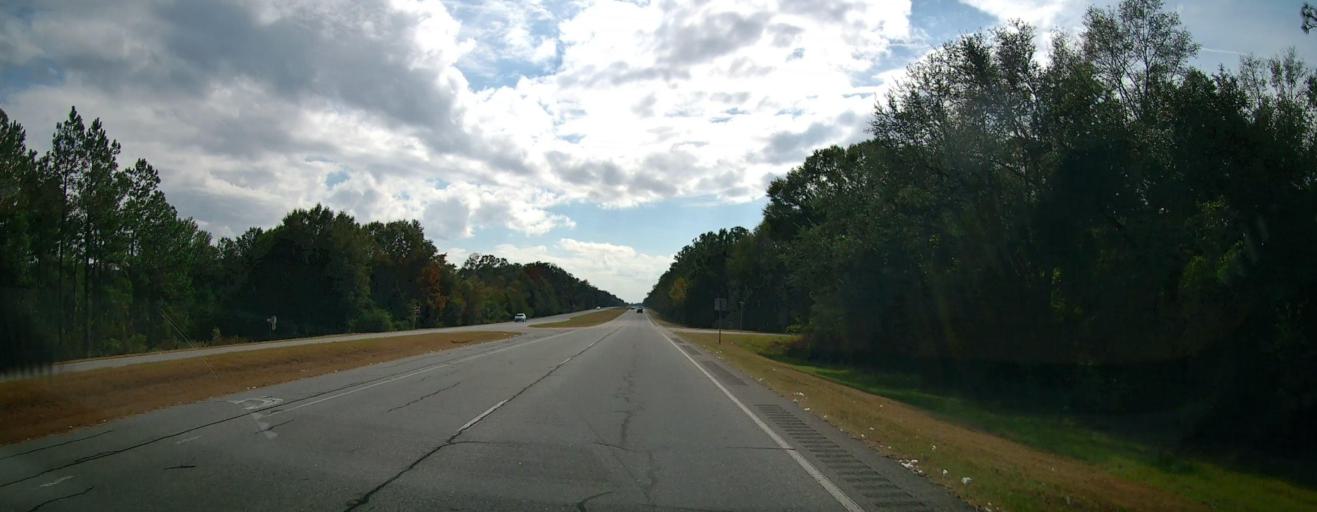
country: US
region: Georgia
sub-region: Mitchell County
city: Camilla
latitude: 31.3099
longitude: -84.1774
